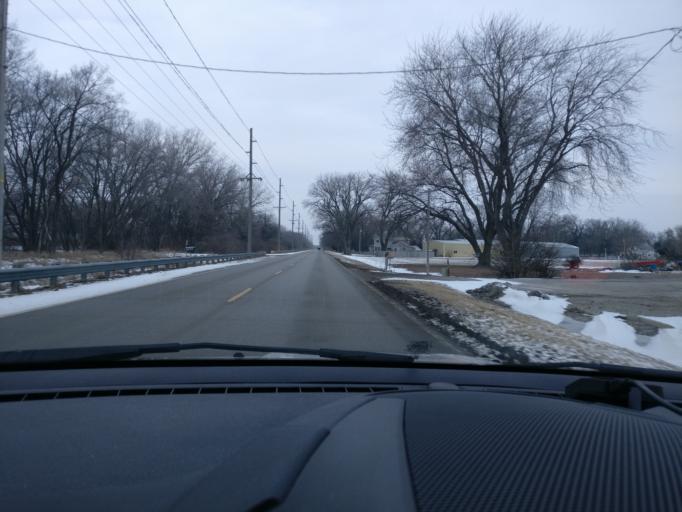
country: US
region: Nebraska
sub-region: Dodge County
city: Fremont
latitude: 41.4401
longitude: -96.5284
